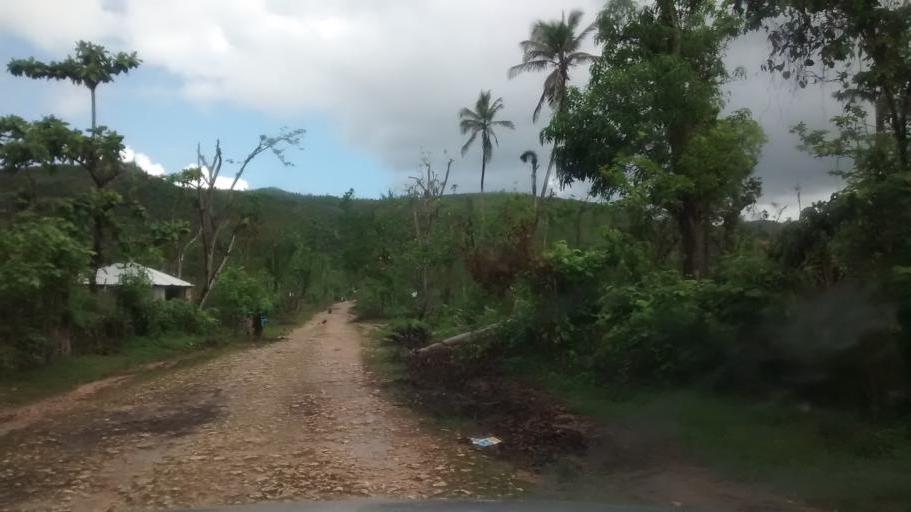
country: HT
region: Grandans
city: Corail
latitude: 18.5357
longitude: -73.9376
